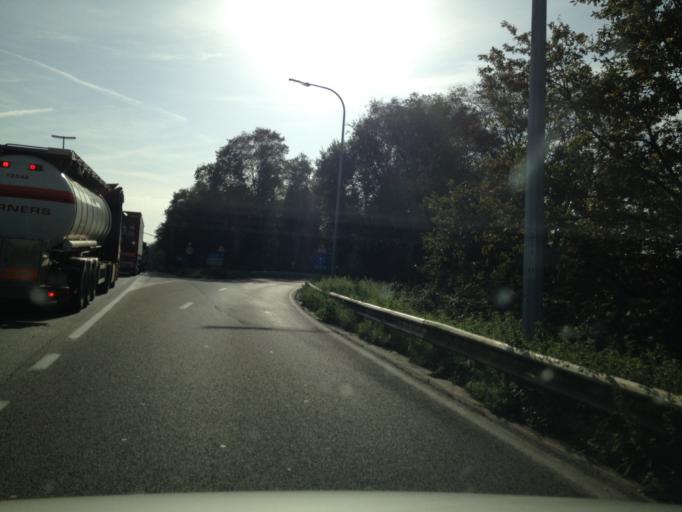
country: BE
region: Flanders
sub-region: Provincie West-Vlaanderen
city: Brugge
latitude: 51.2157
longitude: 3.1888
